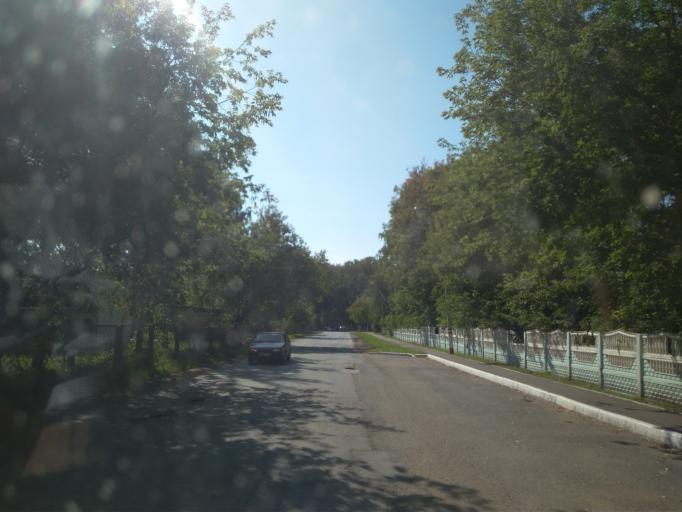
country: RU
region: Mordoviya
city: Saransk
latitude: 54.1892
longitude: 45.1523
